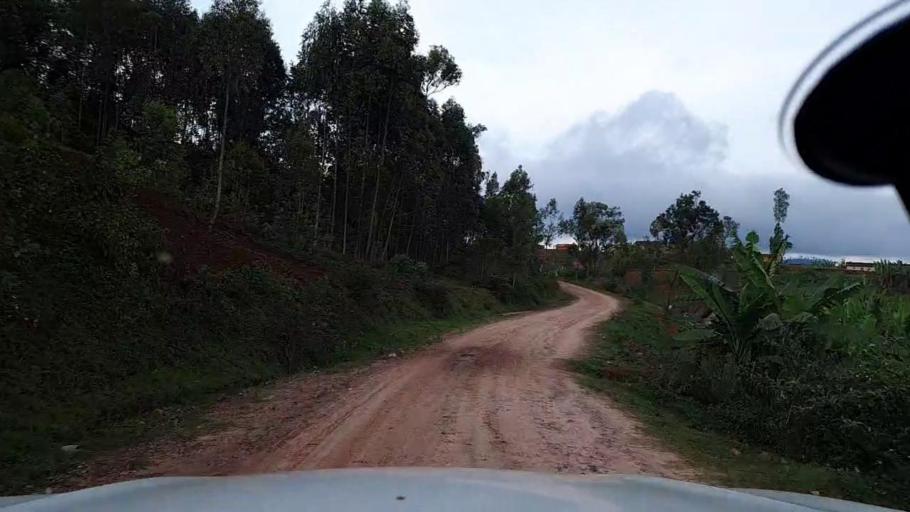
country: RW
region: Southern Province
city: Gitarama
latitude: -2.2091
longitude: 29.6031
